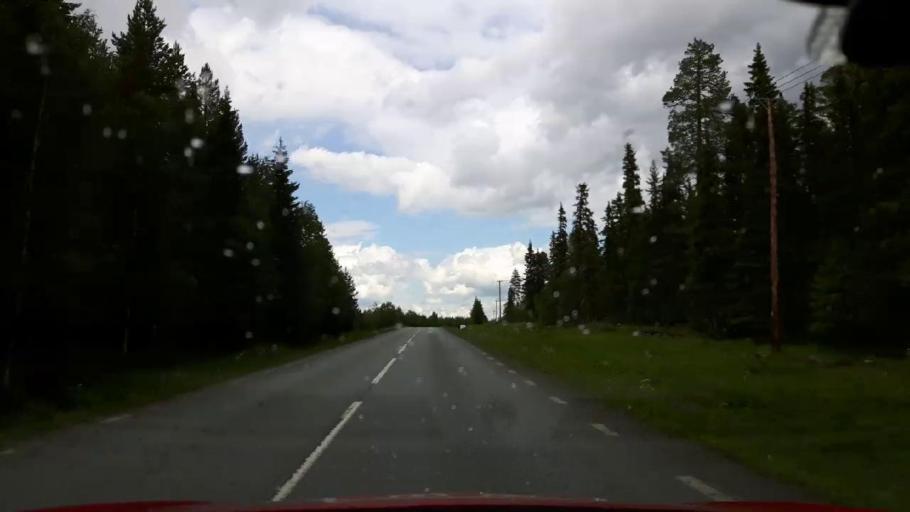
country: SE
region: Jaemtland
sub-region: Krokoms Kommun
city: Krokom
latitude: 63.5350
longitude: 14.2513
